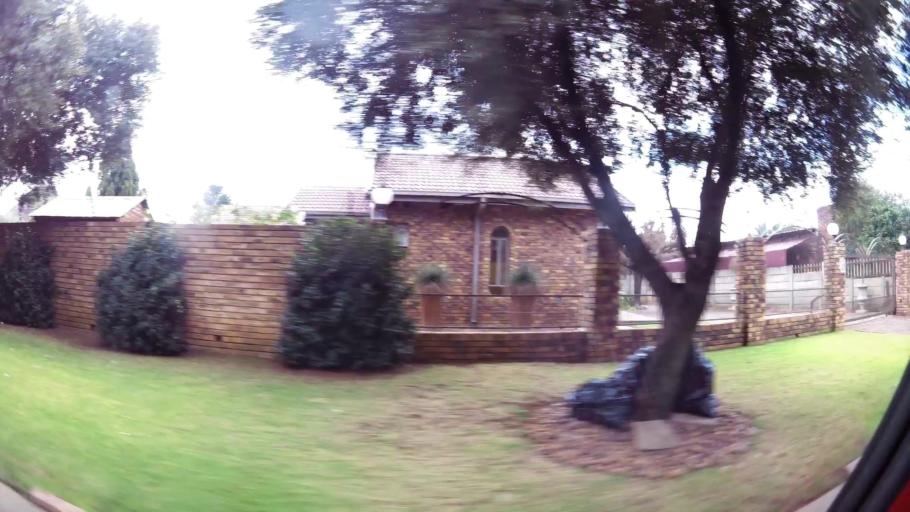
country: ZA
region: Gauteng
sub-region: Sedibeng District Municipality
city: Vanderbijlpark
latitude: -26.7358
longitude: 27.8509
